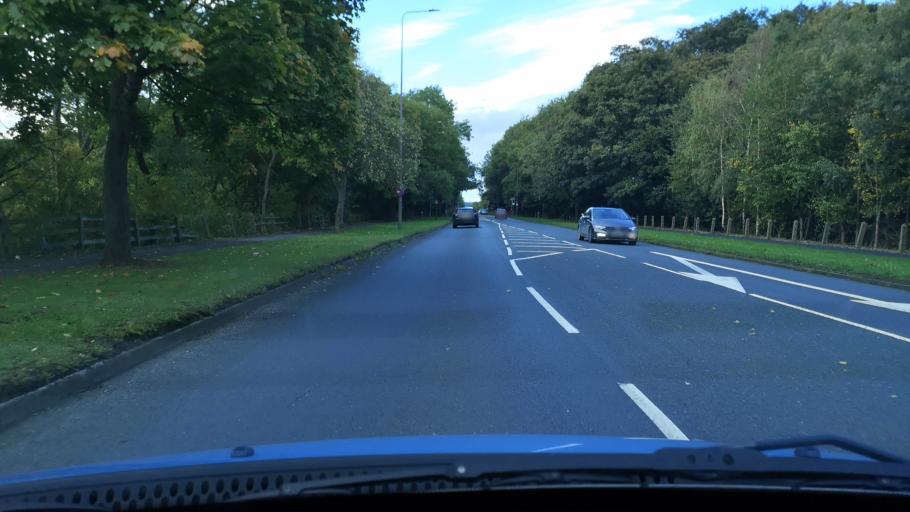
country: GB
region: England
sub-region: North Lincolnshire
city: Scunthorpe
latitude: 53.5815
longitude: -0.6697
